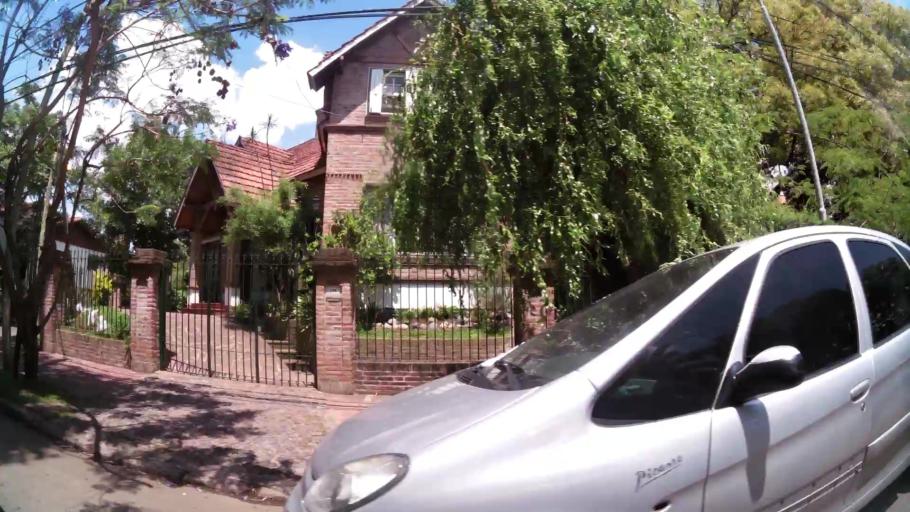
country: AR
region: Buenos Aires
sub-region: Partido de Tigre
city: Tigre
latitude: -34.4221
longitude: -58.5850
